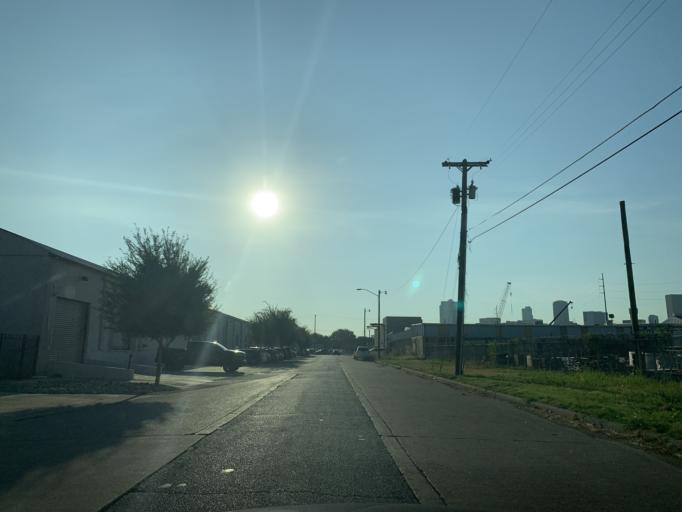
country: US
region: Texas
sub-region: Tarrant County
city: Fort Worth
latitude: 32.7602
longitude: -97.3512
